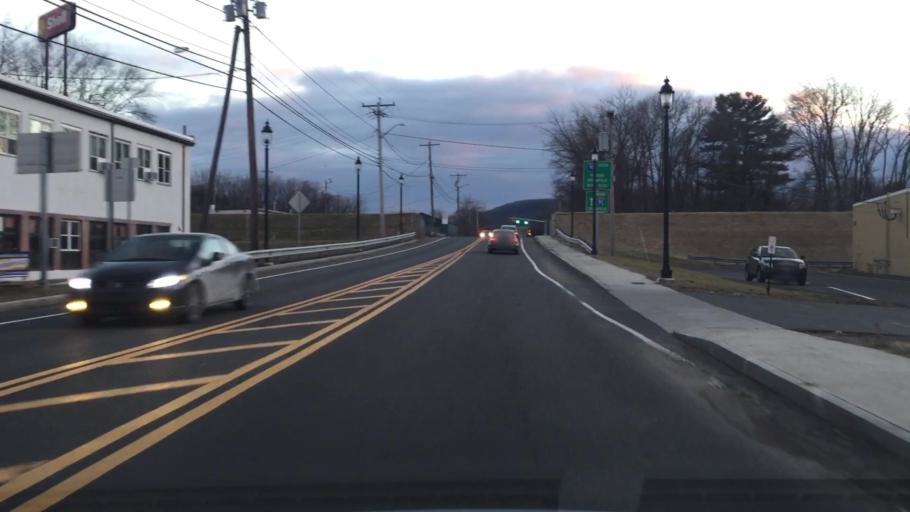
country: US
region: Massachusetts
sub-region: Hampshire County
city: Northampton
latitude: 42.3111
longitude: -72.6242
